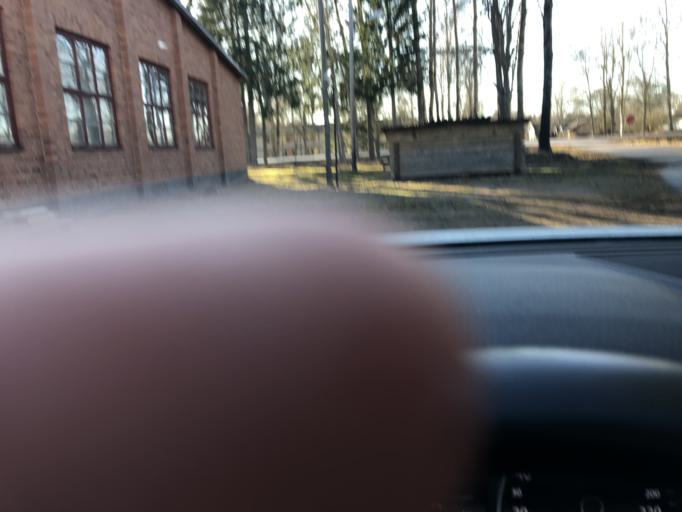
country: SE
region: Uppsala
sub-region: Heby Kommun
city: Tarnsjo
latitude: 60.2916
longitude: 16.8932
